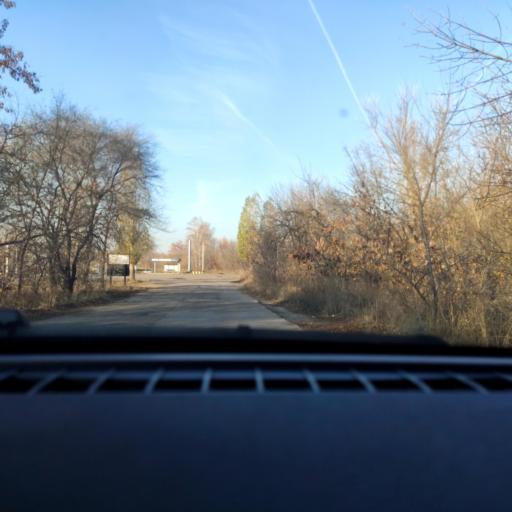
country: RU
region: Voronezj
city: Novaya Usman'
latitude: 51.6391
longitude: 39.3098
